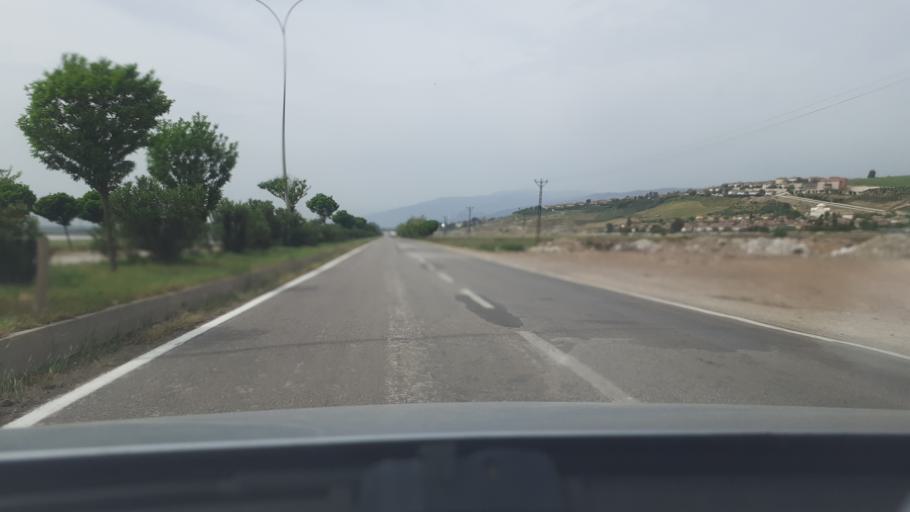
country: TR
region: Hatay
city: Kirikhan
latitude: 36.4784
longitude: 36.3540
